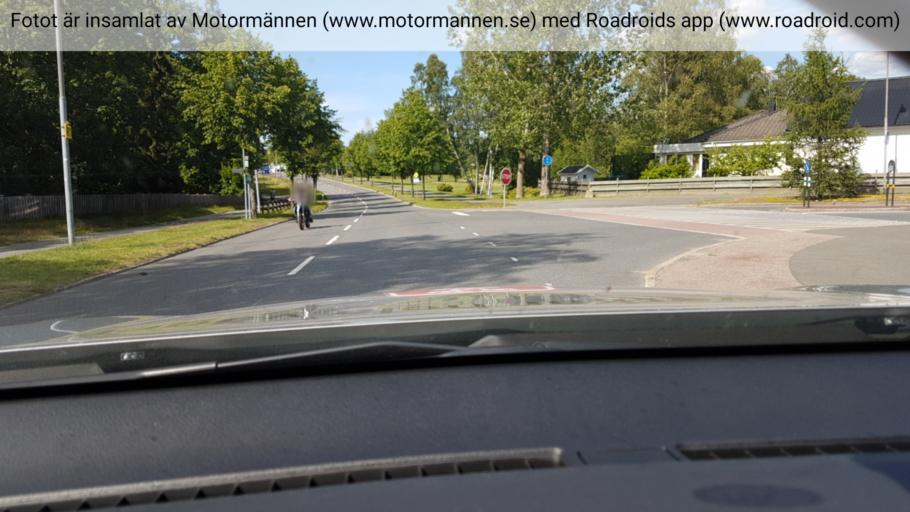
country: SE
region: Joenkoeping
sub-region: Vaggeryds Kommun
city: Vaggeryd
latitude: 57.5028
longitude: 14.1428
